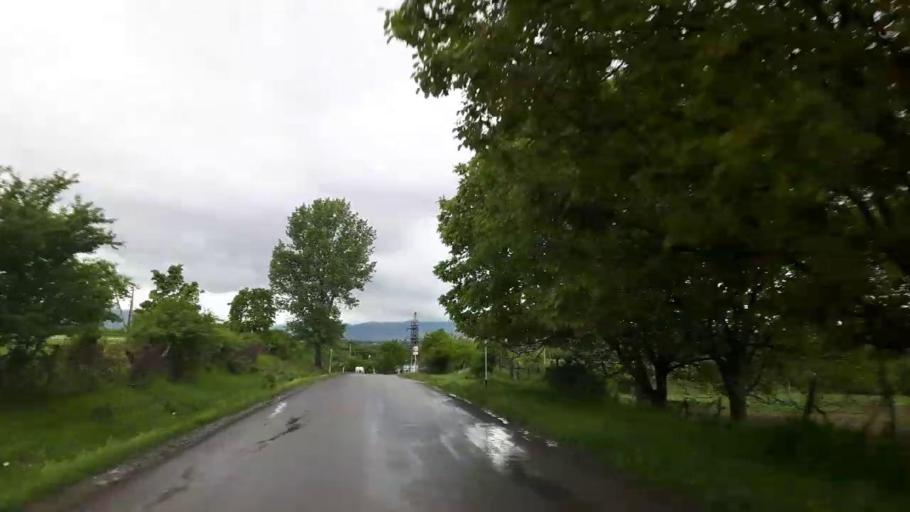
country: GE
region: Shida Kartli
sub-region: Khashuris Raioni
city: Khashuri
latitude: 41.9876
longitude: 43.6613
